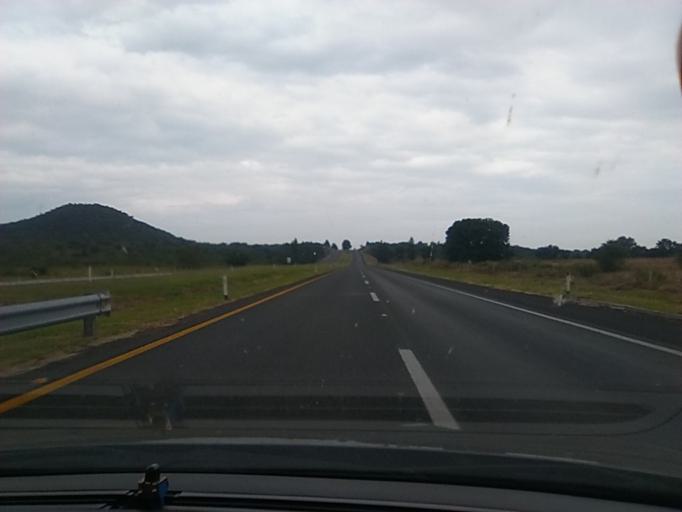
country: MX
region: Michoacan
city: Penjamillo de Degollado
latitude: 20.0006
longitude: -101.8819
